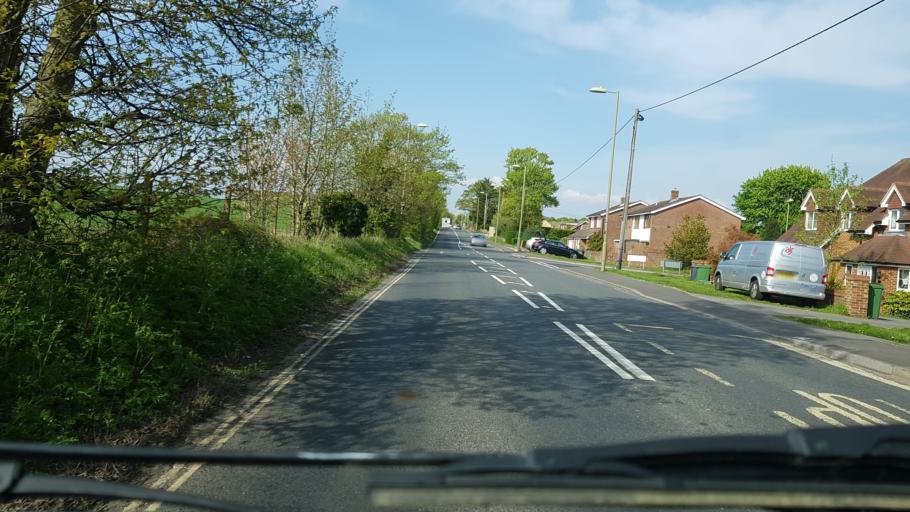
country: GB
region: England
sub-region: Hampshire
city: Basingstoke
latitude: 51.2718
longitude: -1.1292
